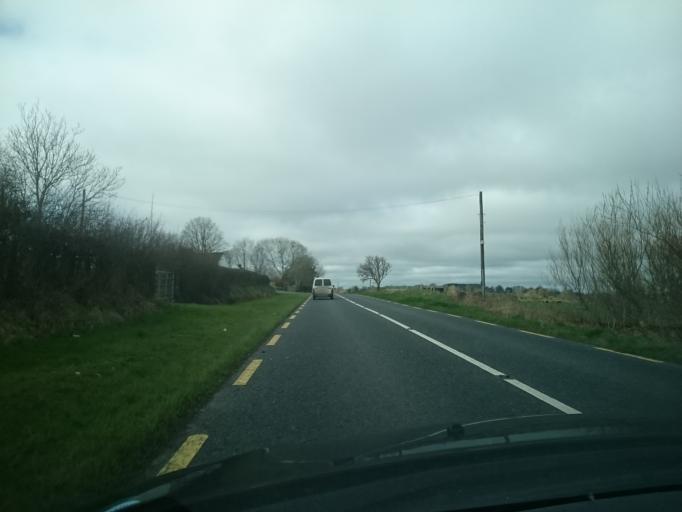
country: IE
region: Connaught
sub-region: Maigh Eo
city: Claremorris
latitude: 53.7199
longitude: -8.9289
